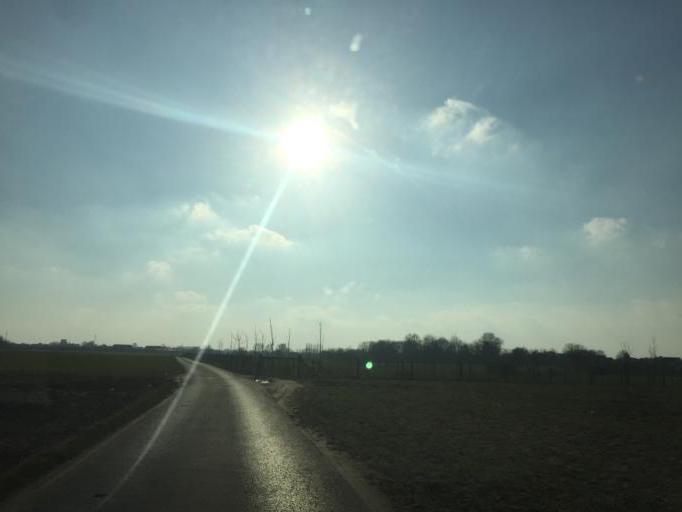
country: BE
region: Flanders
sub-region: Provincie West-Vlaanderen
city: Roeselare
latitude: 50.9166
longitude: 3.1494
